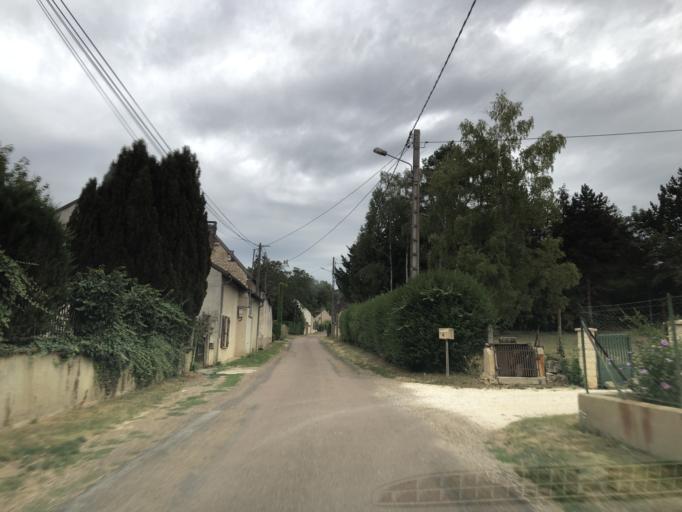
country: FR
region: Bourgogne
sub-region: Departement de l'Yonne
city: Aillant-sur-Tholon
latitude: 47.9040
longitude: 3.3271
